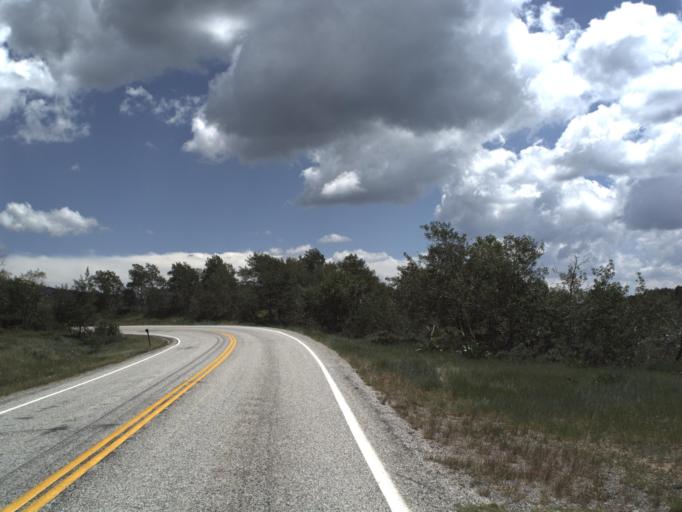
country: US
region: Utah
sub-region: Weber County
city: Wolf Creek
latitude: 41.4088
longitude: -111.5566
